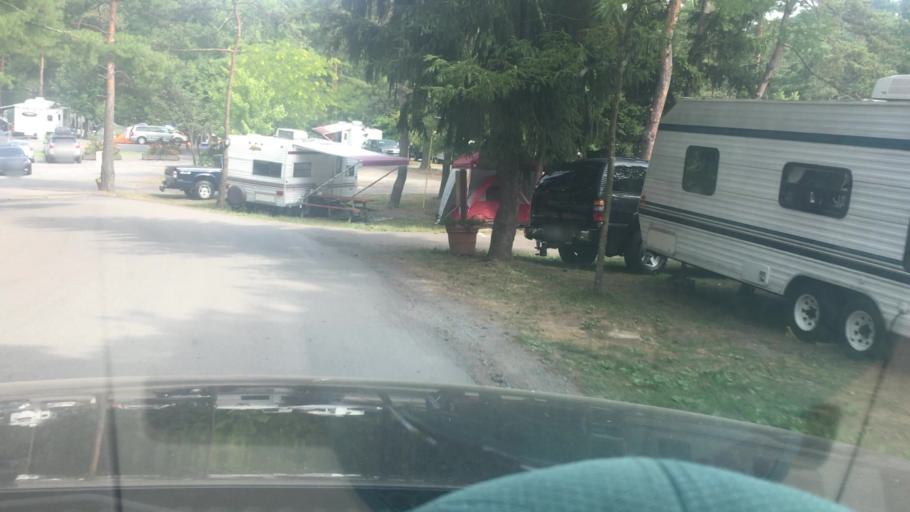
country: US
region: Pennsylvania
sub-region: Northumberland County
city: Elysburg
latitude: 40.8757
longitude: -76.5027
